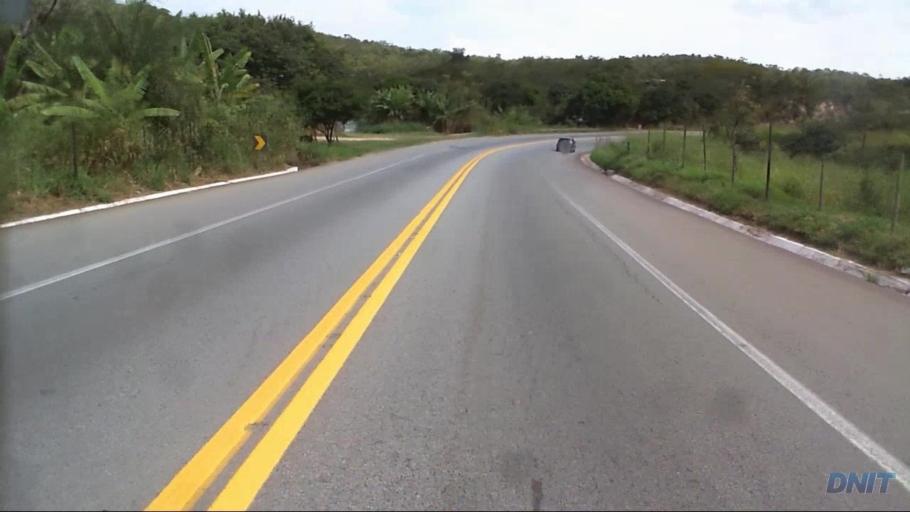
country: BR
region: Minas Gerais
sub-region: Santa Luzia
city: Santa Luzia
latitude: -19.8150
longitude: -43.8011
